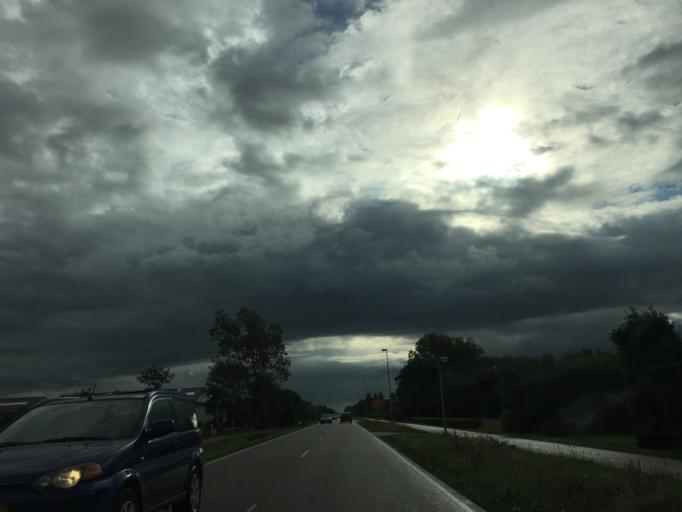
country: NL
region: North Holland
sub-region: Gemeente Den Helder
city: Den Helder
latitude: 52.9224
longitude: 4.7549
